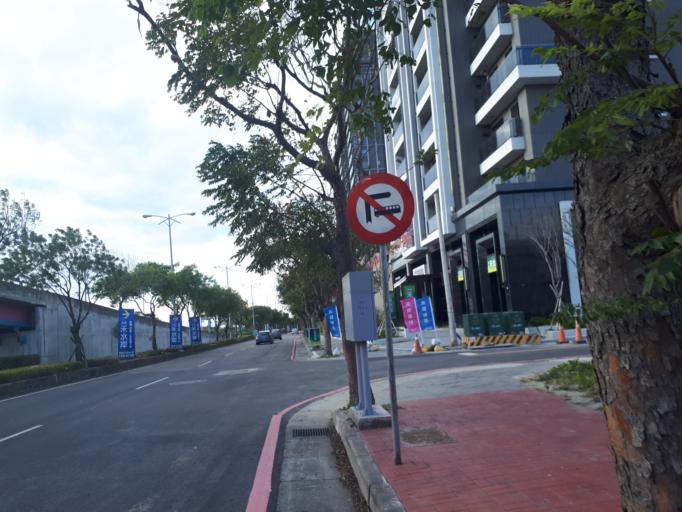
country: TW
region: Taiwan
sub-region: Hsinchu
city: Zhubei
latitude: 24.8004
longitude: 121.0374
